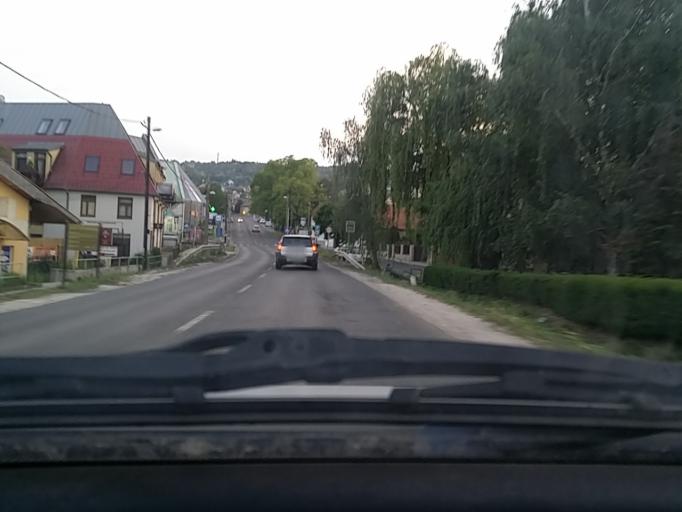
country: HU
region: Pest
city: Solymar
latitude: 47.5929
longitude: 18.9386
